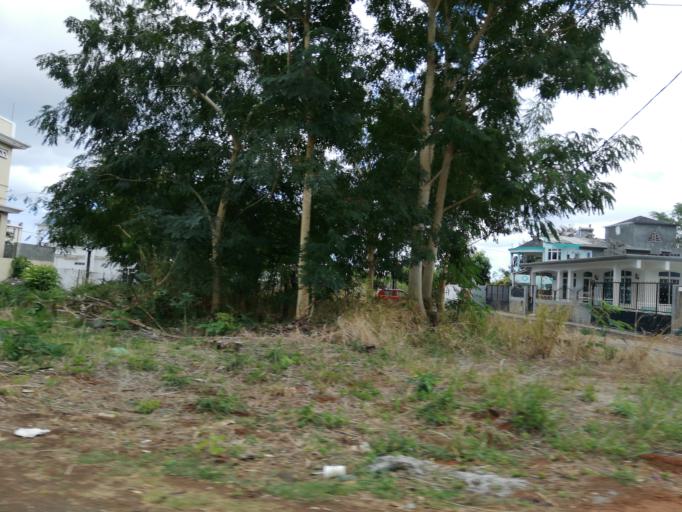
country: MU
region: Pamplemousses
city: Arsenal
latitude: -20.1033
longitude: 57.5432
